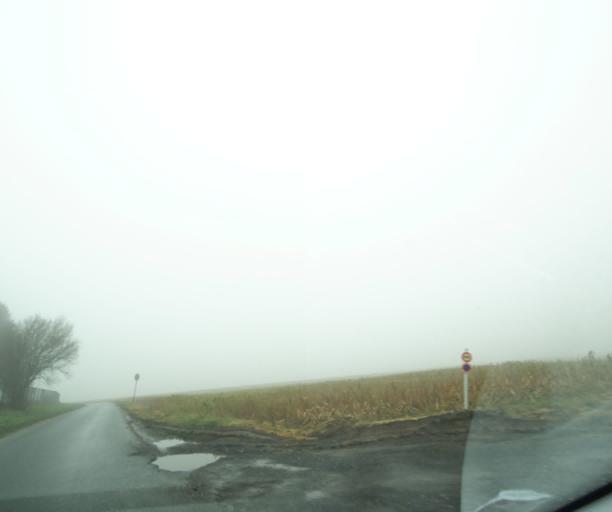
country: FR
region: Ile-de-France
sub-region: Departement de Seine-et-Marne
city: Longperrier
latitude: 49.0464
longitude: 2.6651
